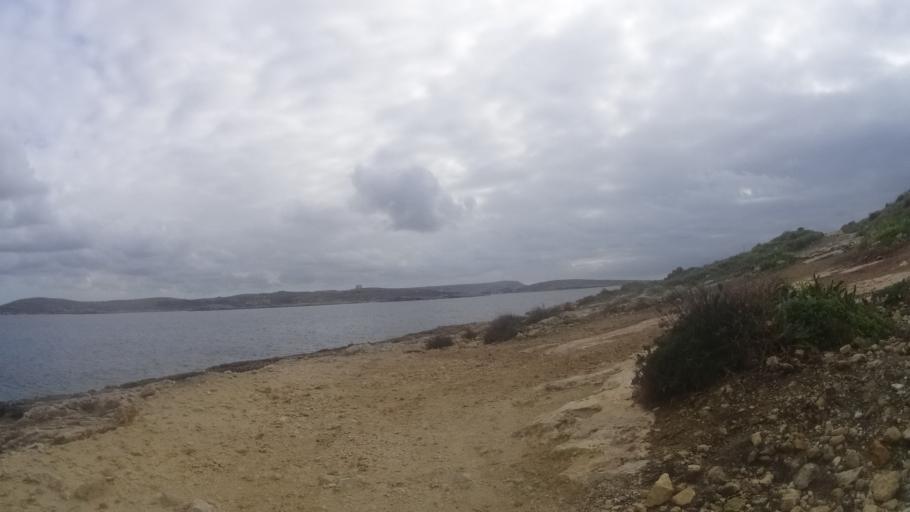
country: MT
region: Il-Qala
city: Qala
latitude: 36.0274
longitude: 14.3220
